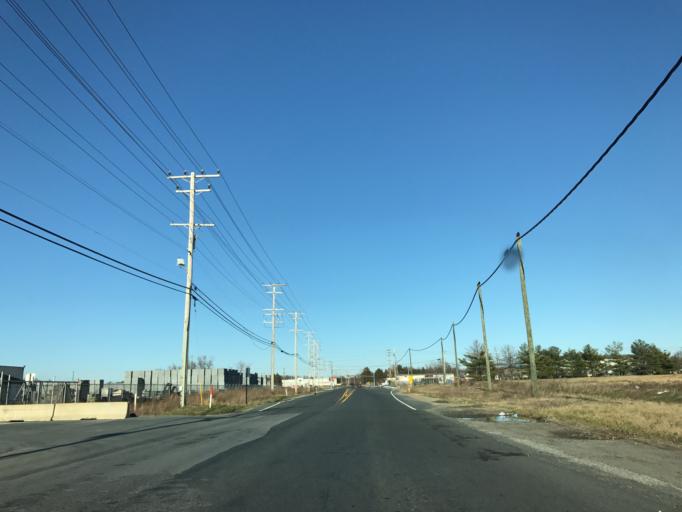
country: US
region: Maryland
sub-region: Harford County
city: Aberdeen
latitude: 39.4907
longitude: -76.1829
